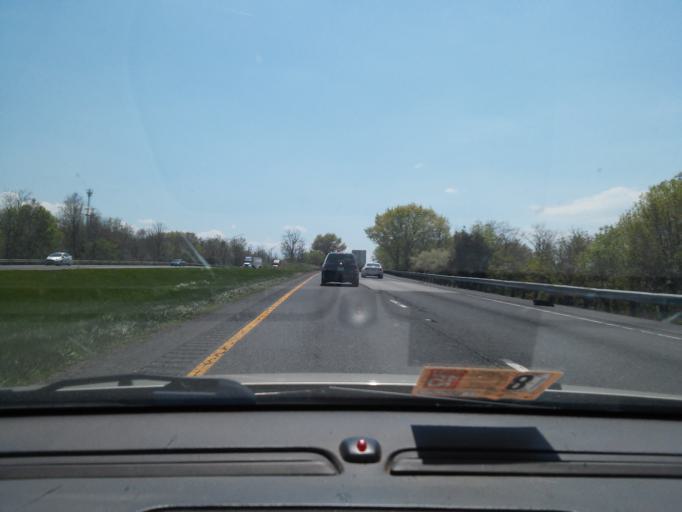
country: US
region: Maryland
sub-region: Washington County
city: Fountainhead-Orchard Hills
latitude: 39.6729
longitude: -77.7349
